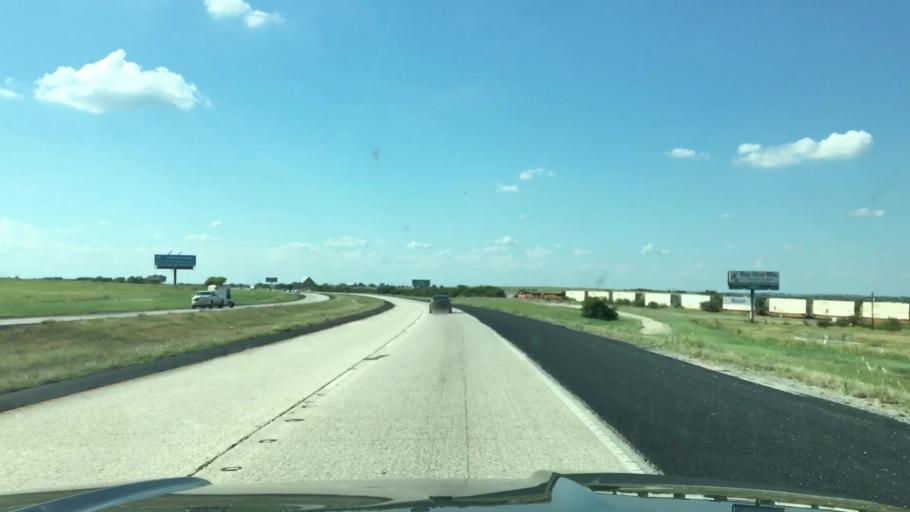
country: US
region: Texas
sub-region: Wise County
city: New Fairview
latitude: 33.1436
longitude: -97.4995
